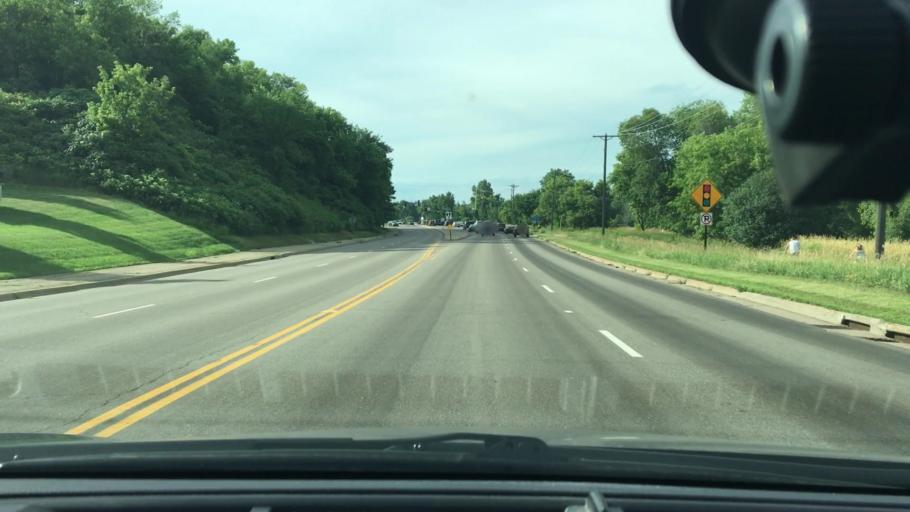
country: US
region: Minnesota
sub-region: Hennepin County
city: Plymouth
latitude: 45.0265
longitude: -93.4438
